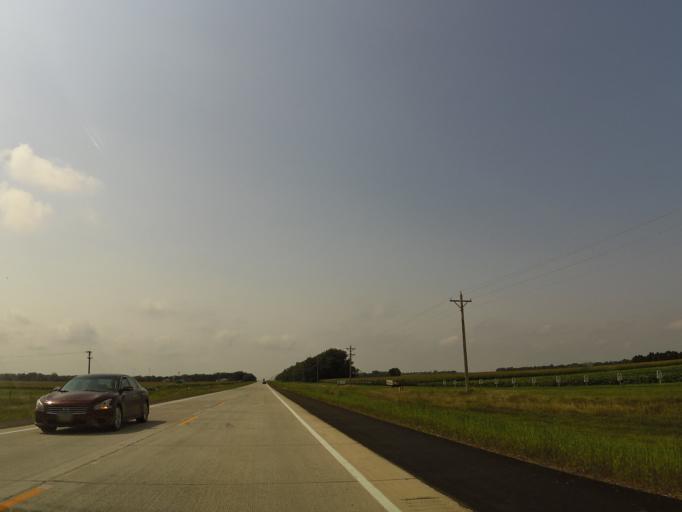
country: US
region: South Dakota
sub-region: Codington County
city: Watertown
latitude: 44.8901
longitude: -97.0051
